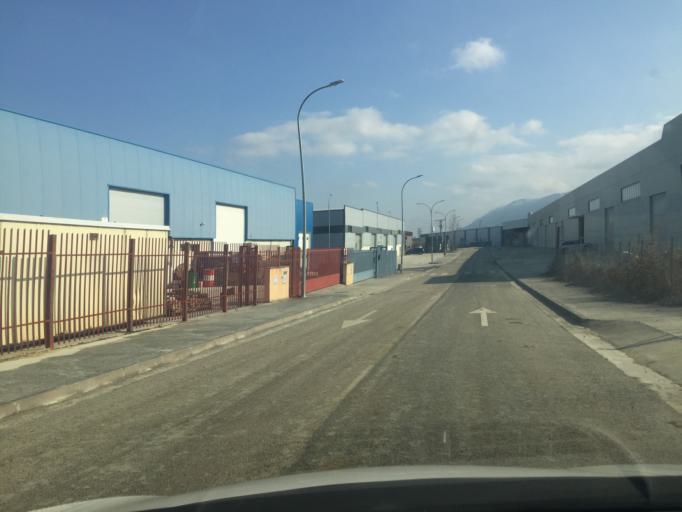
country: ES
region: Castille and Leon
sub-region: Provincia de Burgos
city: Medina de Pomar
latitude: 42.9248
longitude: -3.5848
